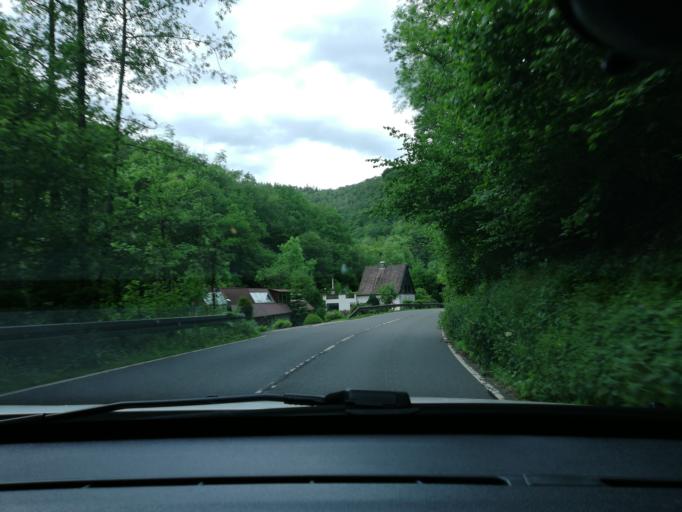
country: DE
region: North Rhine-Westphalia
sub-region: Regierungsbezirk Arnsberg
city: Schalksmuhle
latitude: 51.2353
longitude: 7.5562
